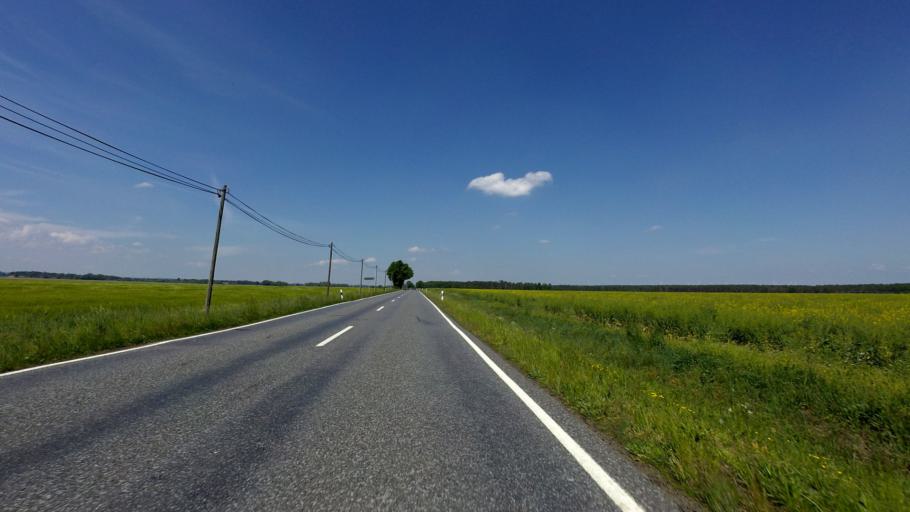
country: DE
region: Brandenburg
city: Luckau
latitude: 51.8238
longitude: 13.7914
